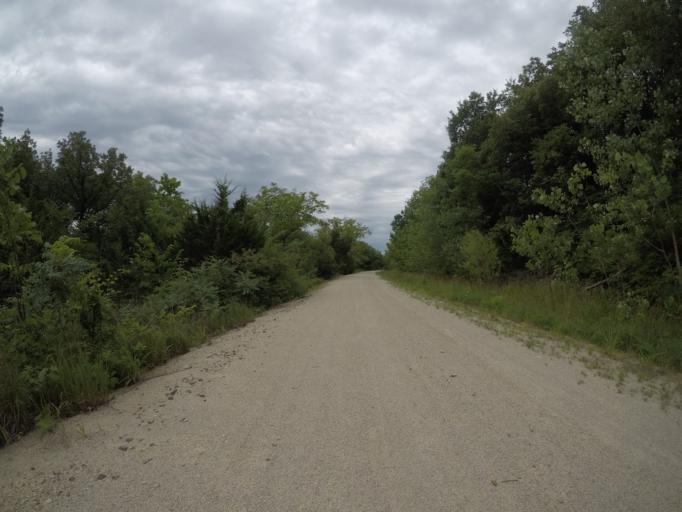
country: US
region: Kansas
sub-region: Anderson County
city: Garnett
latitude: 38.3240
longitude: -95.2471
